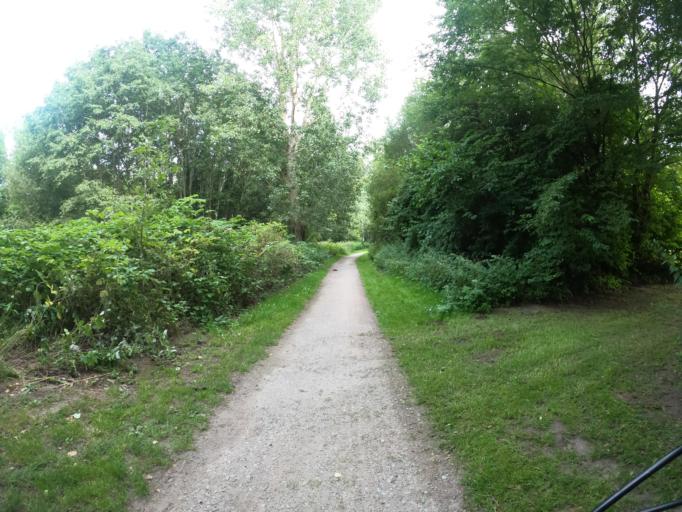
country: DE
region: North Rhine-Westphalia
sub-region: Regierungsbezirk Arnsberg
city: Lippstadt
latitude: 51.6941
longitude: 8.3296
